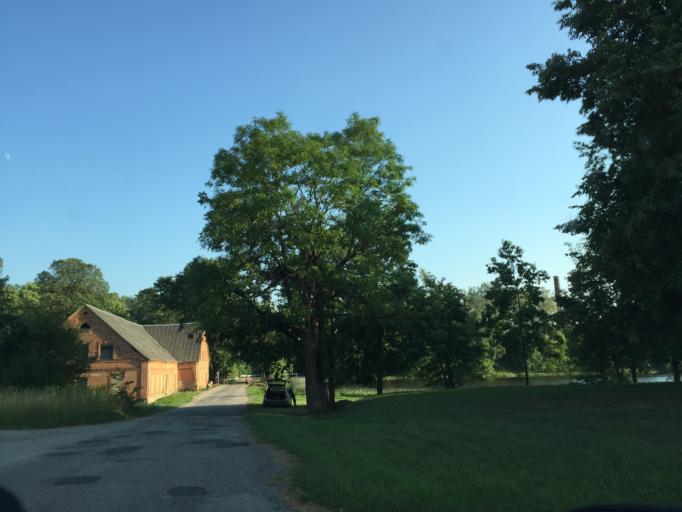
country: LV
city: Tervete
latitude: 56.4313
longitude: 23.4799
